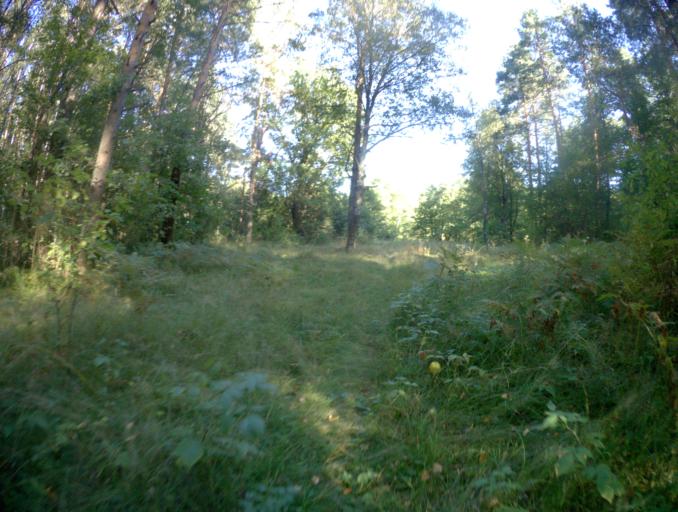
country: RU
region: Vladimir
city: Krasnaya Gorbatka
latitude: 55.7895
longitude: 41.6608
